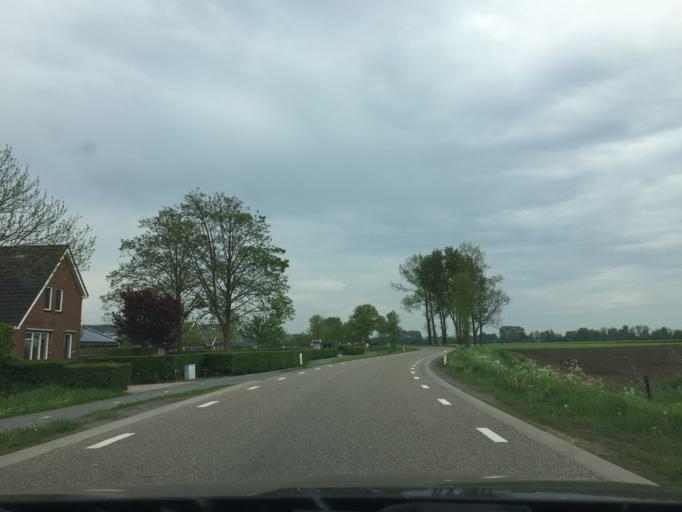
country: NL
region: Groningen
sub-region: Gemeente Zuidhorn
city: Aduard
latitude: 53.2691
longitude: 6.4350
